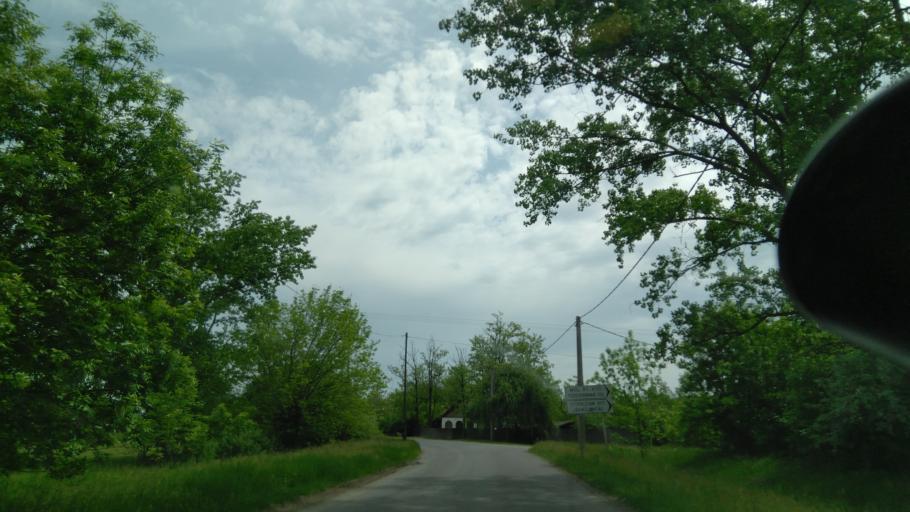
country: HU
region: Bekes
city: Fuzesgyarmat
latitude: 47.0981
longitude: 21.2303
